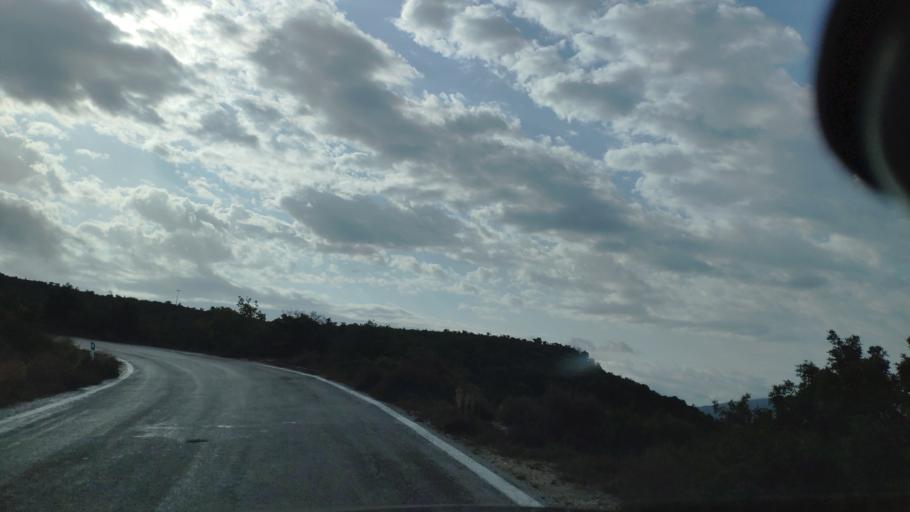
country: GR
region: West Greece
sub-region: Nomos Aitolias kai Akarnanias
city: Sardinia
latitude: 38.8878
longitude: 21.2403
